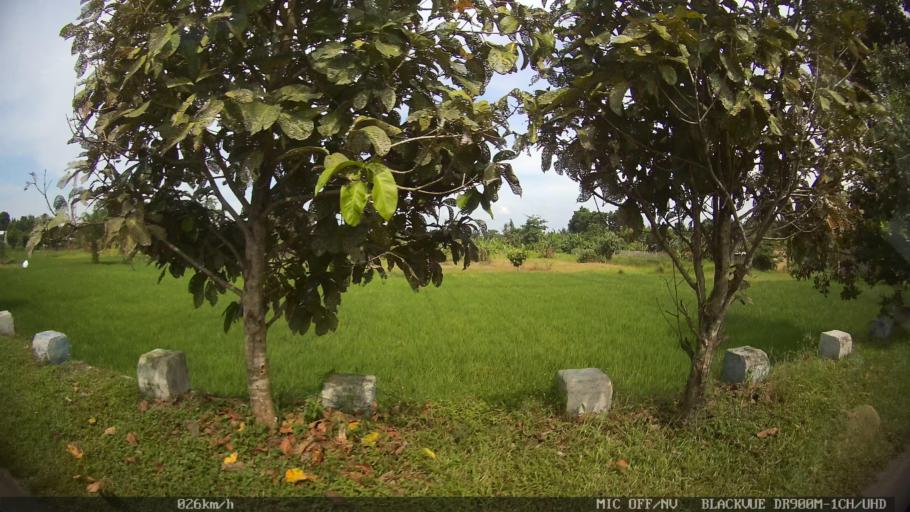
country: ID
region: North Sumatra
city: Percut
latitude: 3.6132
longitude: 98.8308
